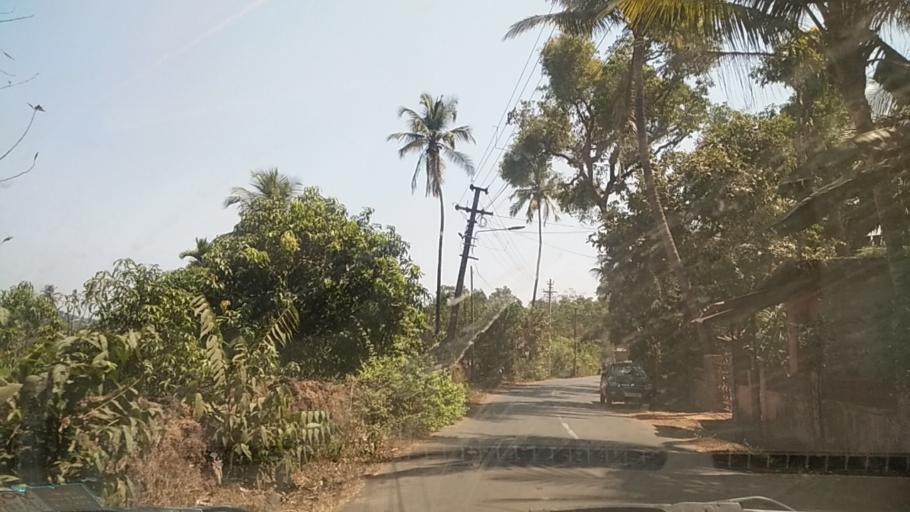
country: IN
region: Goa
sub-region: North Goa
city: Dicholi
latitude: 15.5772
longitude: 73.9171
